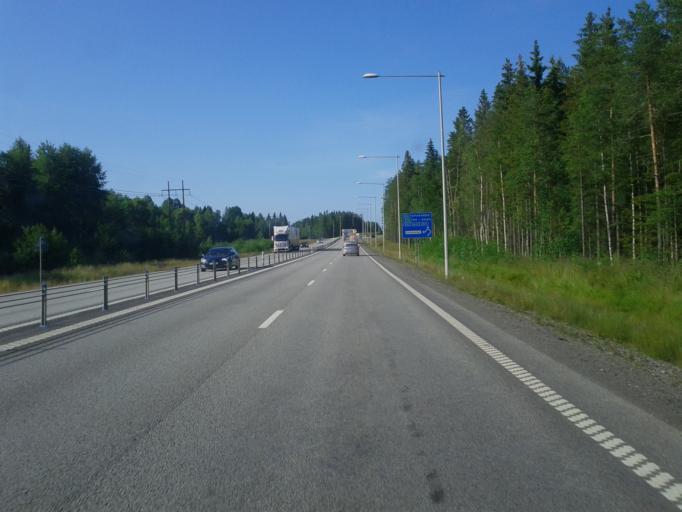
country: SE
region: Vaesterbotten
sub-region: Umea Kommun
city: Umea
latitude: 63.8125
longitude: 20.3267
